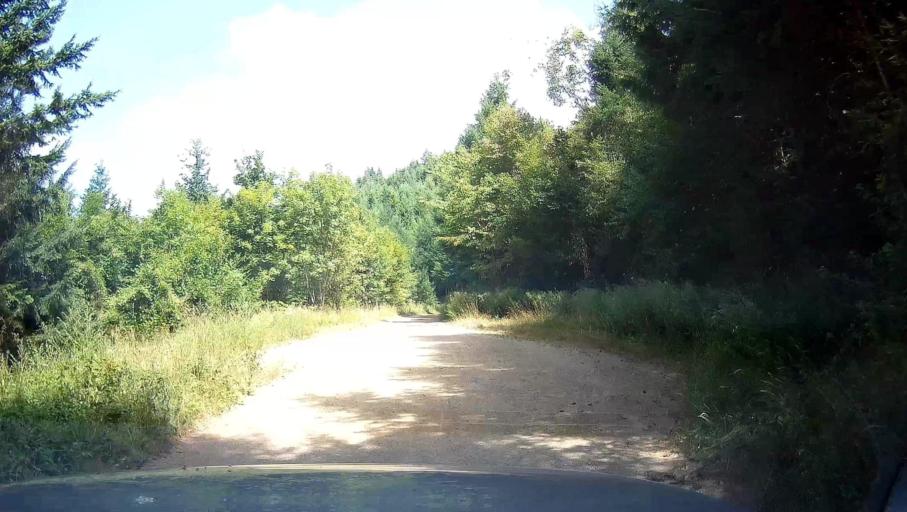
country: FR
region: Rhone-Alpes
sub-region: Departement du Rhone
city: Grandris
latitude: 46.0195
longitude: 4.5386
